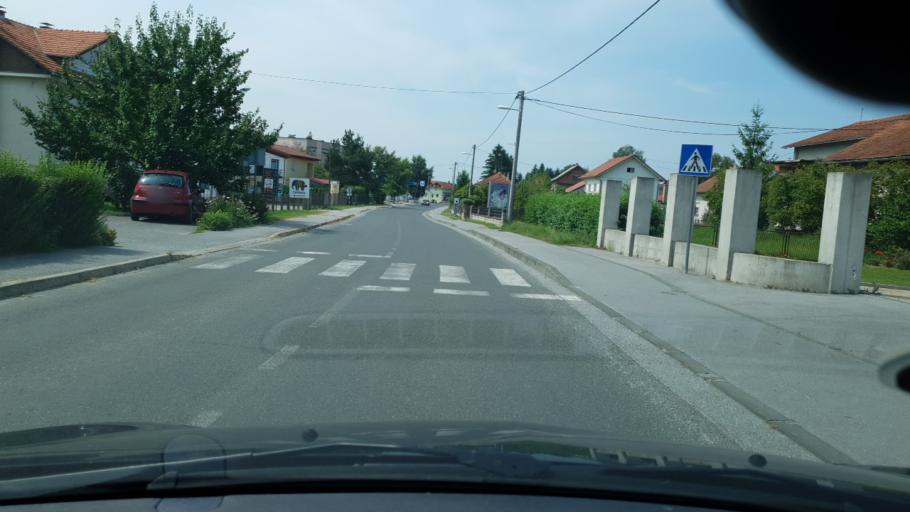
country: HR
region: Krapinsko-Zagorska
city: Bedekovcina
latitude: 46.0417
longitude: 15.9938
